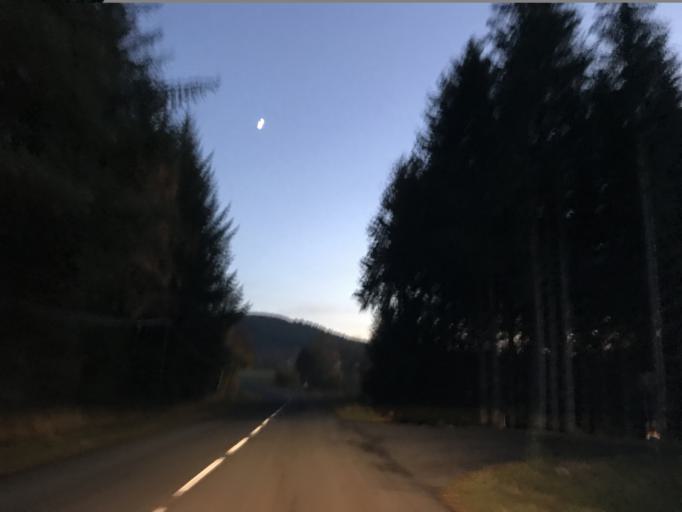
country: FR
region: Rhone-Alpes
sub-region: Departement de la Loire
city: Noiretable
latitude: 45.7759
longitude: 3.6798
